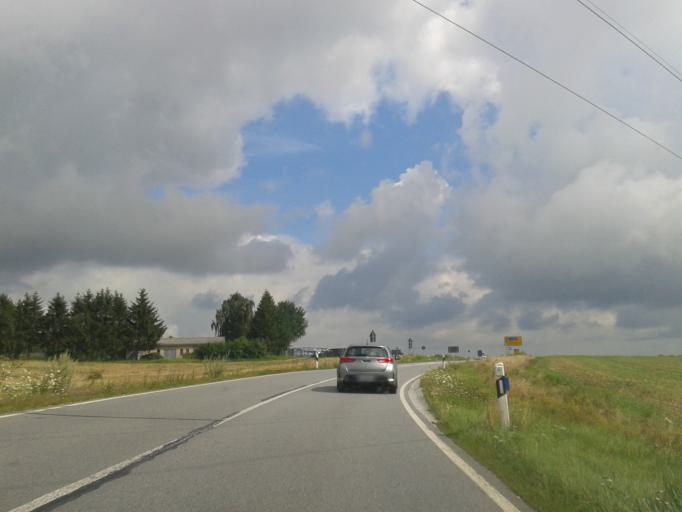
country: DE
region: Saxony
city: Radeberg
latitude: 51.0722
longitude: 13.9329
